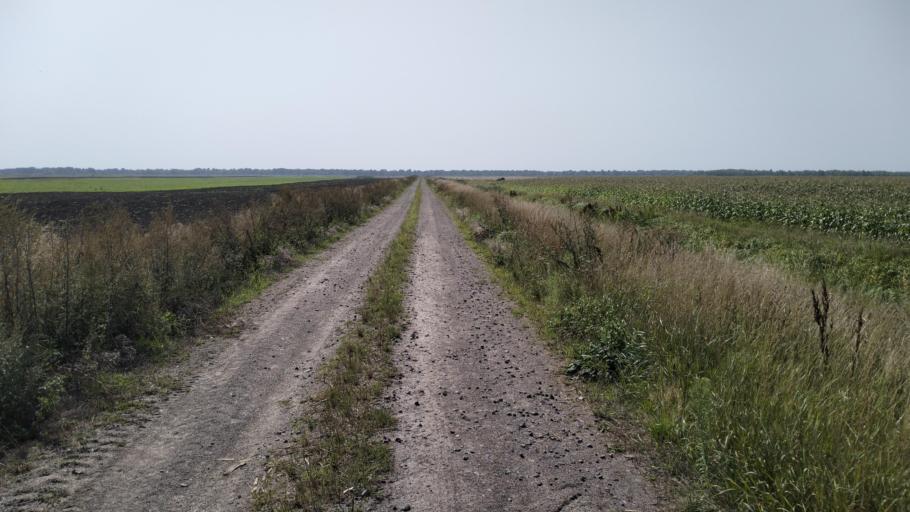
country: BY
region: Brest
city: Davyd-Haradok
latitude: 51.9859
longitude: 27.1639
